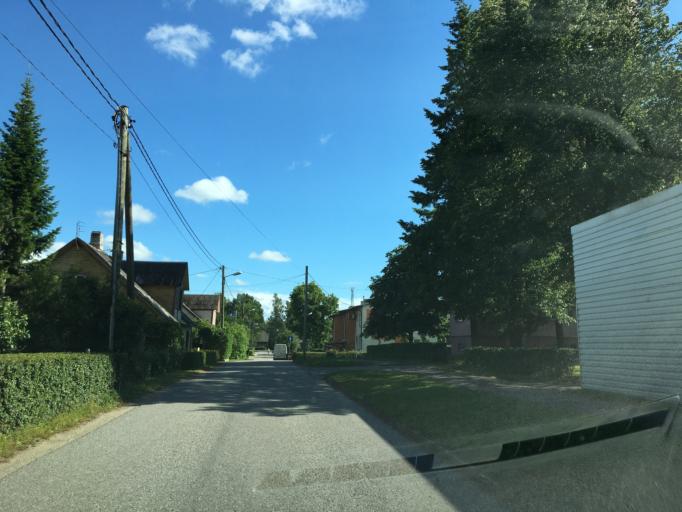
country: EE
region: Paernumaa
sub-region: Vaendra vald (alev)
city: Vandra
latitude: 58.6541
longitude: 25.0388
